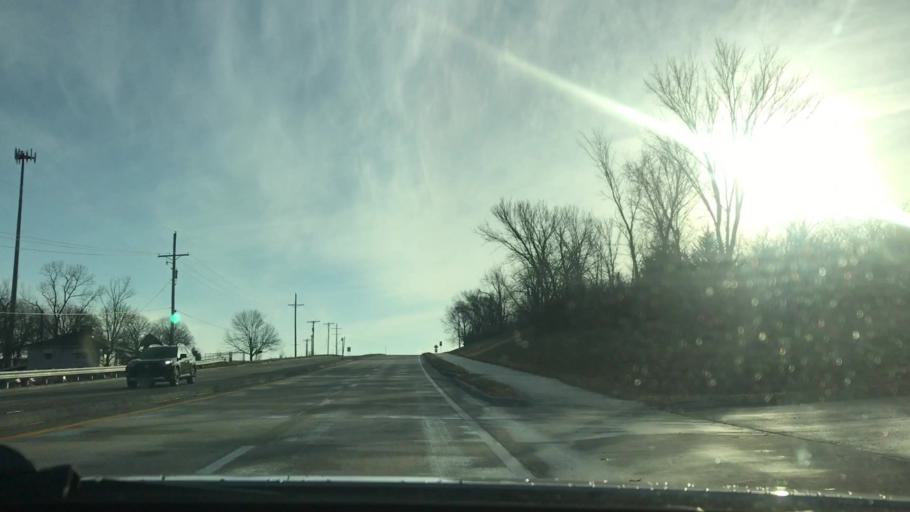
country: US
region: Missouri
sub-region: Platte County
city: Weatherby Lake
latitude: 39.2213
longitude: -94.7398
